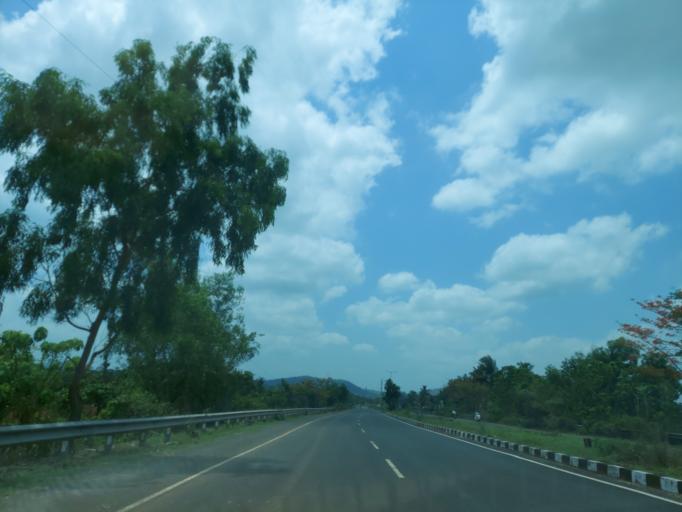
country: IN
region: Maharashtra
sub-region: Sindhudurg
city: Savantvadi
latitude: 15.8233
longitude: 73.8561
